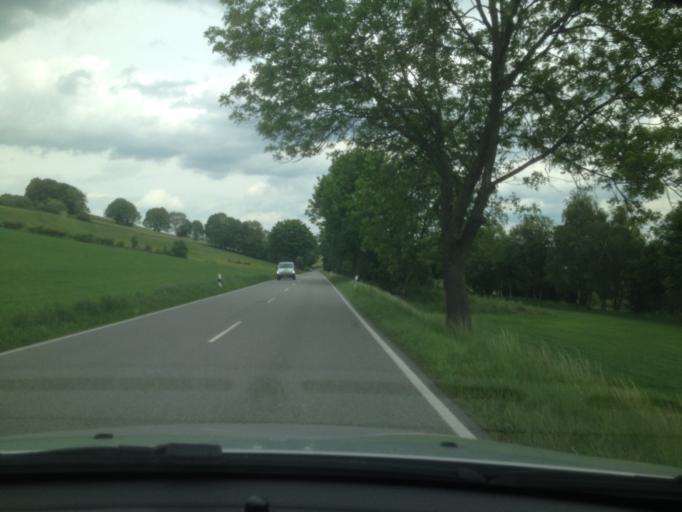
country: DE
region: Saxony
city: Lossnitz
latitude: 50.6474
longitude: 12.7532
